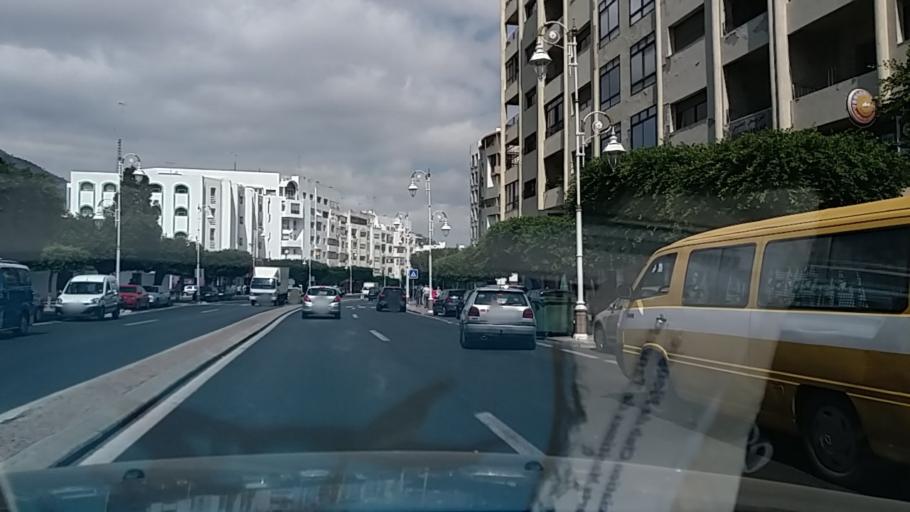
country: MA
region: Tanger-Tetouan
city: Tetouan
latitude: 35.5727
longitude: -5.3599
